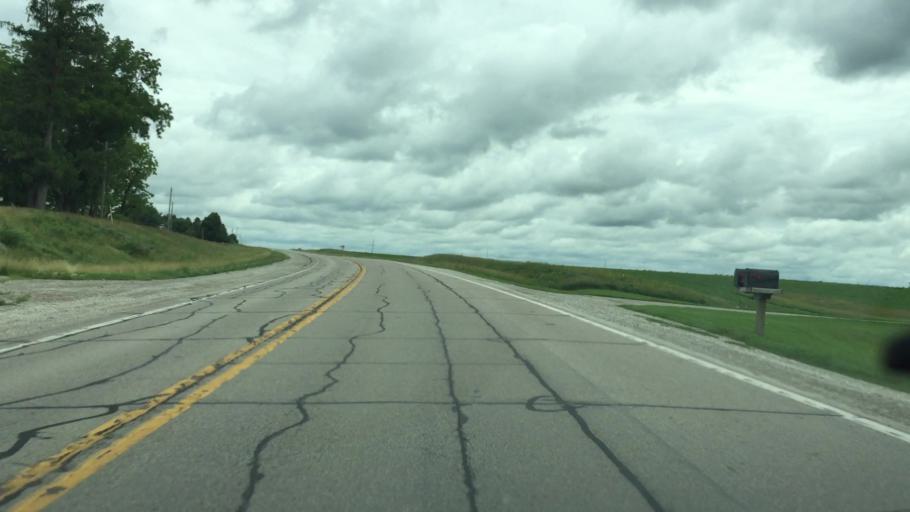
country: US
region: Iowa
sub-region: Jasper County
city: Monroe
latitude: 41.5468
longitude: -93.0971
